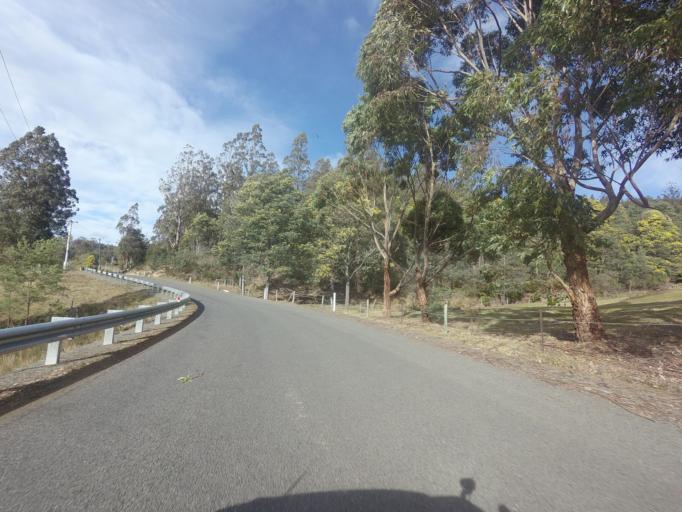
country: AU
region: Tasmania
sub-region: Kingborough
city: Margate
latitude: -43.0137
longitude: 147.1599
